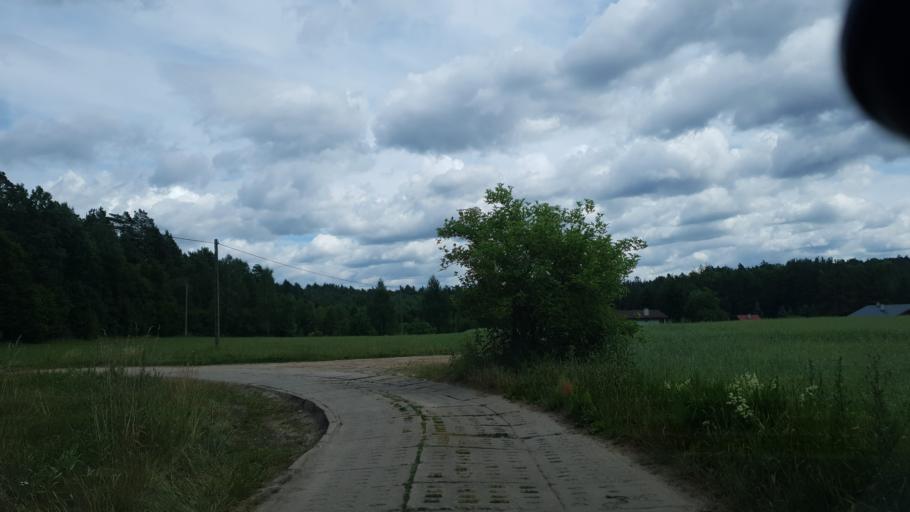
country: PL
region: Pomeranian Voivodeship
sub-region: Powiat kartuski
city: Stezyca
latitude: 54.2482
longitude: 17.9964
